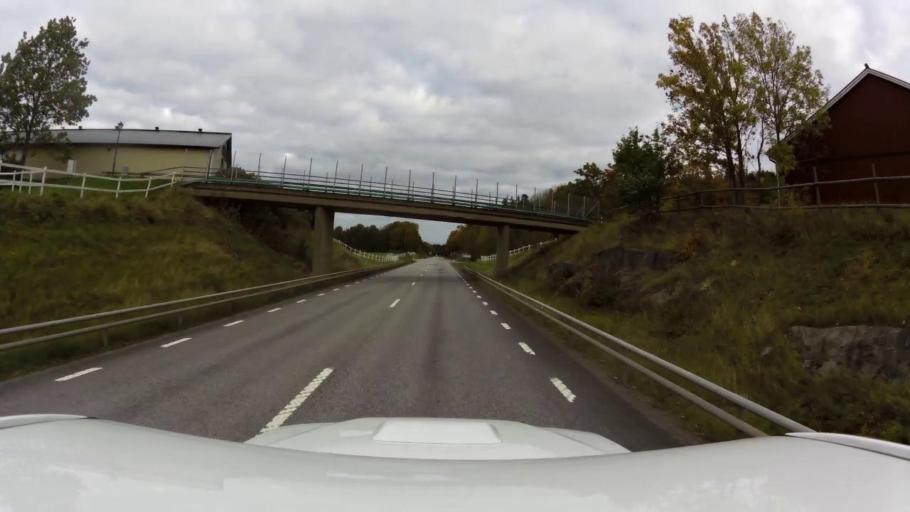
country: SE
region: OEstergoetland
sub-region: Kinda Kommun
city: Rimforsa
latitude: 58.1730
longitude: 15.6765
